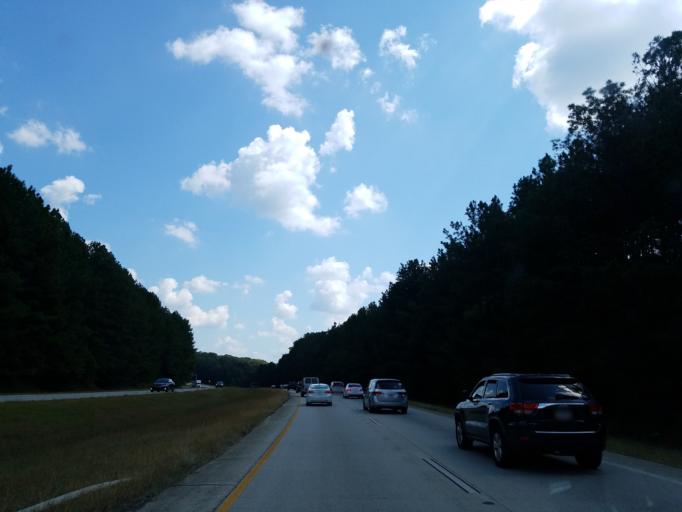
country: US
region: Georgia
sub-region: Gwinnett County
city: Dacula
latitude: 33.9757
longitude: -83.9189
